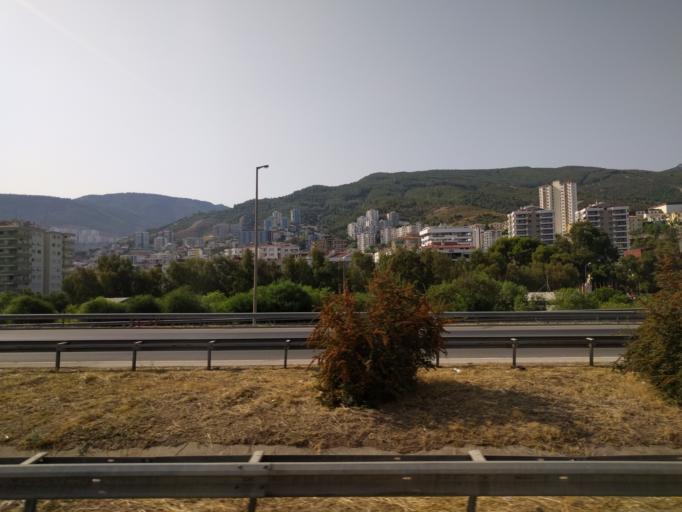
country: TR
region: Izmir
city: Karsiyaka
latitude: 38.3978
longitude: 26.9977
